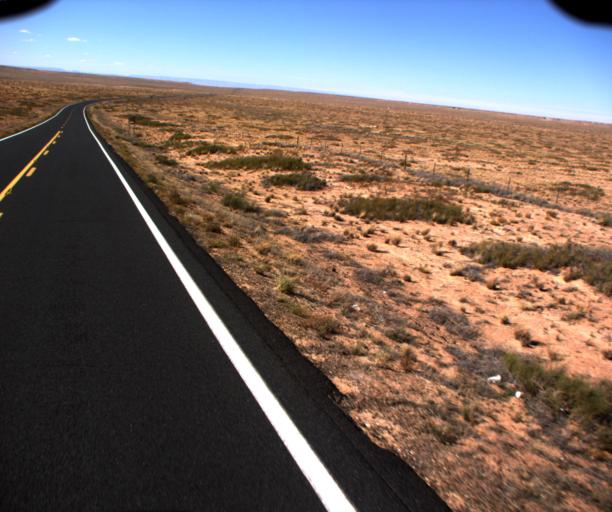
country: US
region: Arizona
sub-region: Coconino County
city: Tuba City
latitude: 36.0202
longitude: -111.1241
